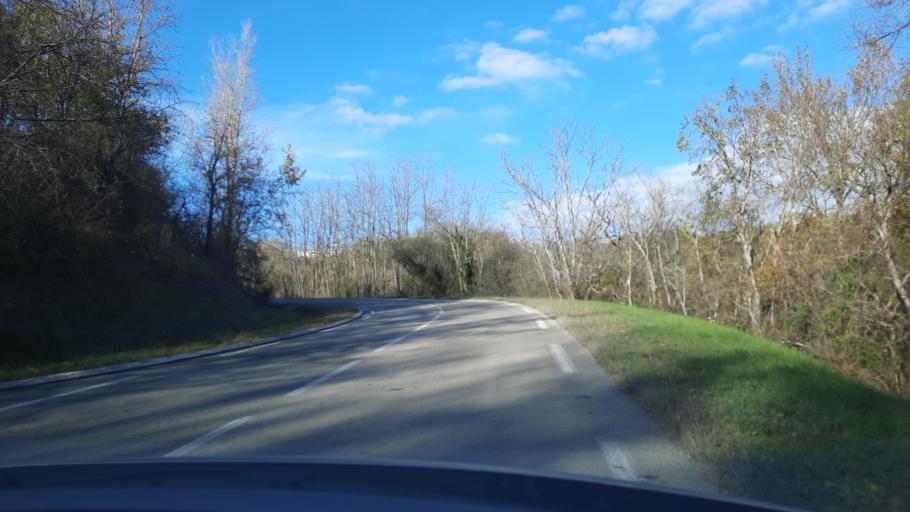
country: FR
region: Midi-Pyrenees
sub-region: Departement du Tarn-et-Garonne
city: Molieres
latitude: 44.1194
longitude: 1.3550
